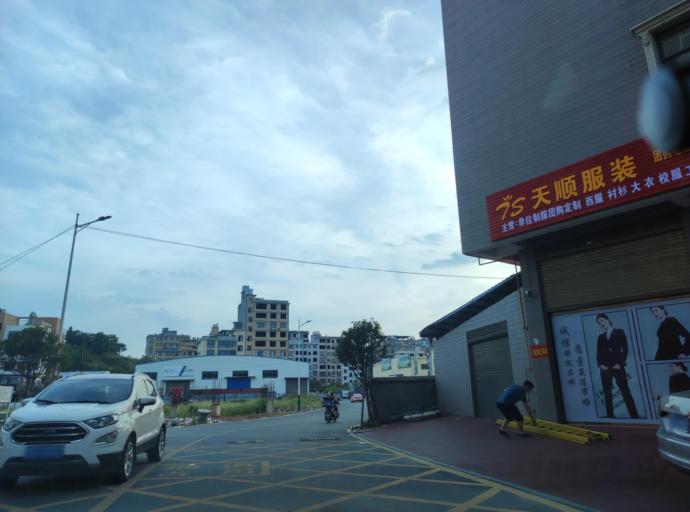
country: CN
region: Jiangxi Sheng
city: Pingxiang
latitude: 27.6422
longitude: 113.8801
